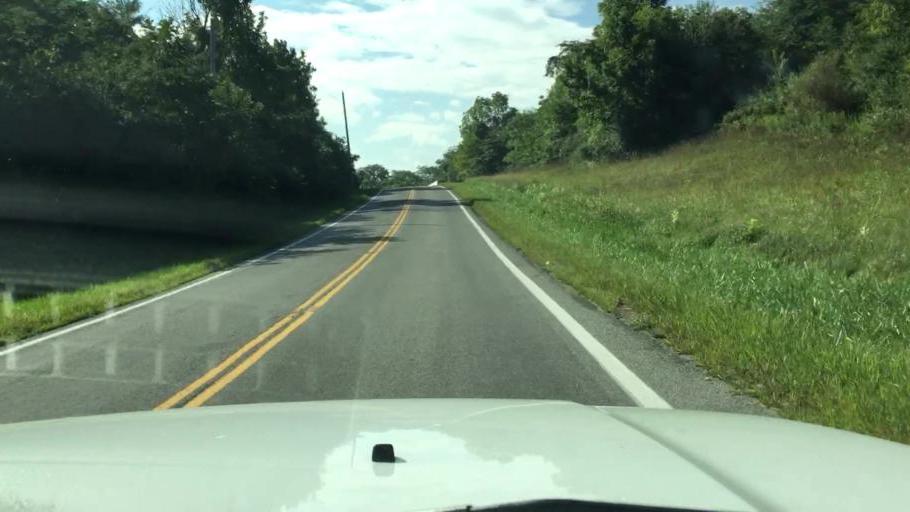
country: US
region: Ohio
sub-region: Champaign County
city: Mechanicsburg
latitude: 40.0401
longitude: -83.6052
